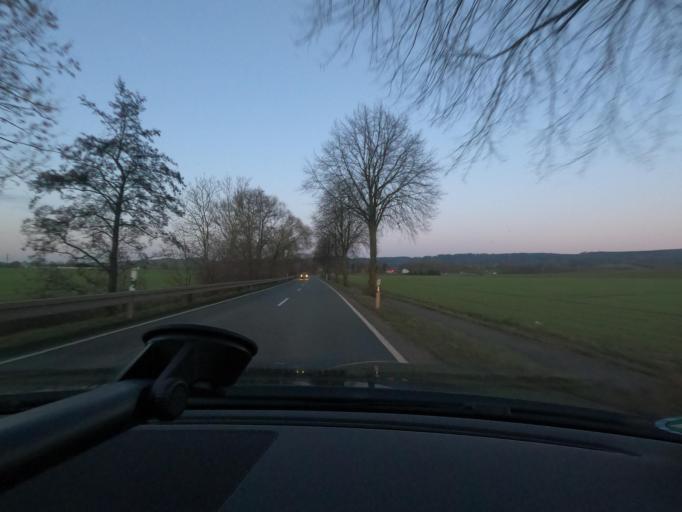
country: DE
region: Lower Saxony
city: Badenhausen
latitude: 51.7781
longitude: 10.1935
